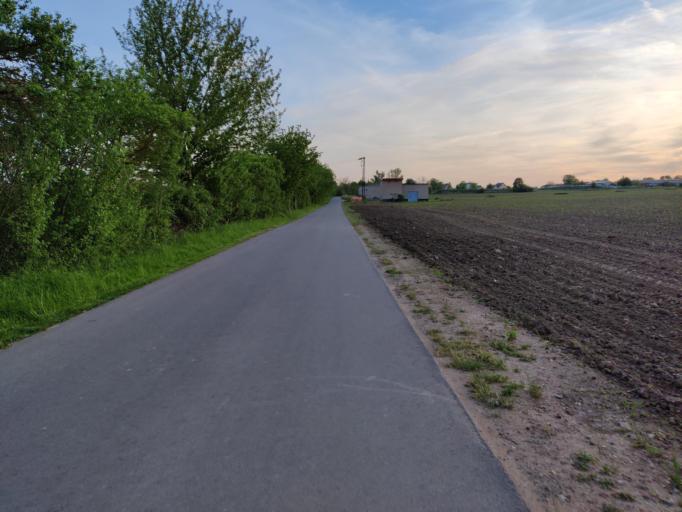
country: DE
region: Saxony-Anhalt
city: Karsdorf
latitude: 51.2493
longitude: 11.6510
